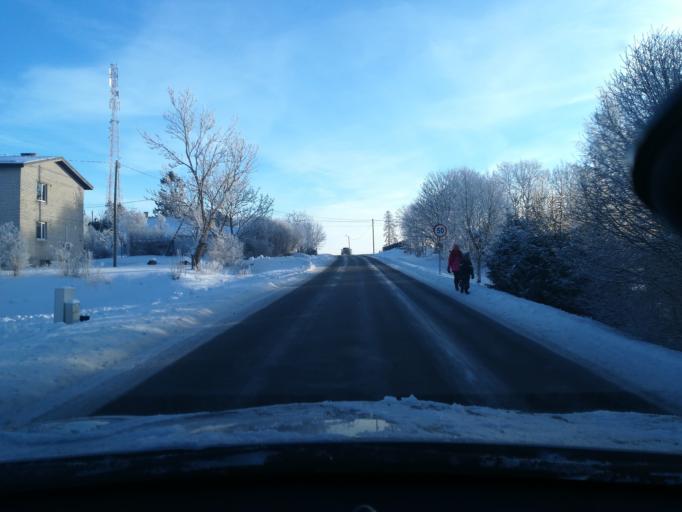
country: EE
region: Harju
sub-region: Saue linn
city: Saue
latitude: 59.3632
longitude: 24.4877
